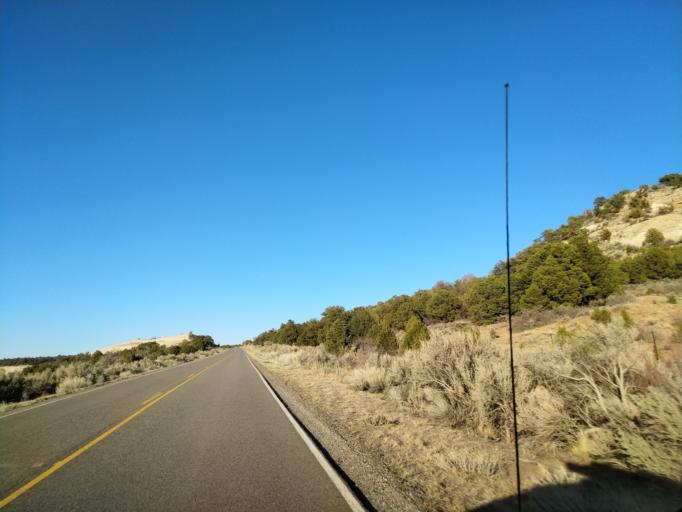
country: US
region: Colorado
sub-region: Mesa County
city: Redlands
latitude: 38.9839
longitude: -108.7928
